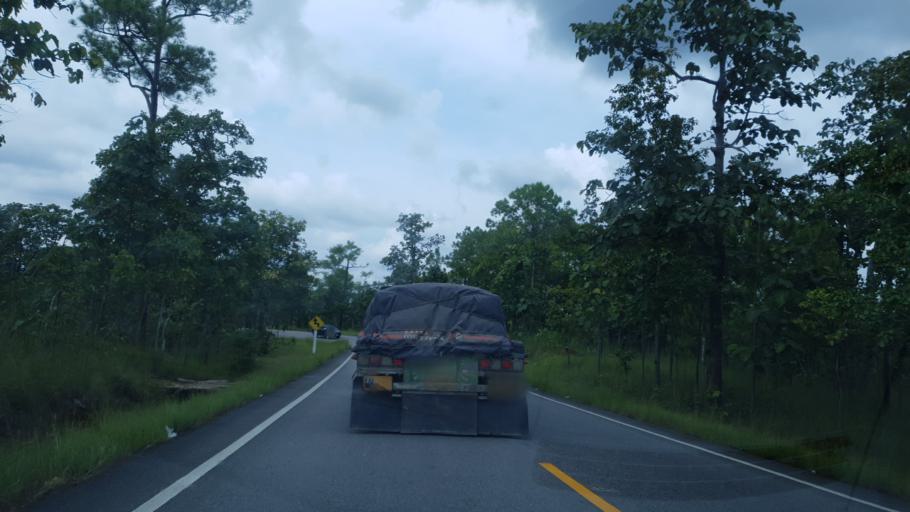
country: TH
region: Mae Hong Son
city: Khun Yuam
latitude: 18.7879
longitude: 97.9374
